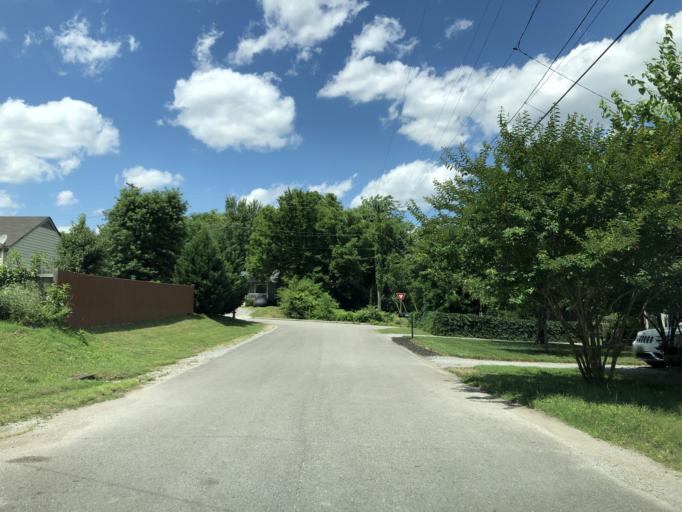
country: US
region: Tennessee
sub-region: Davidson County
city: Nashville
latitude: 36.1856
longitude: -86.7271
